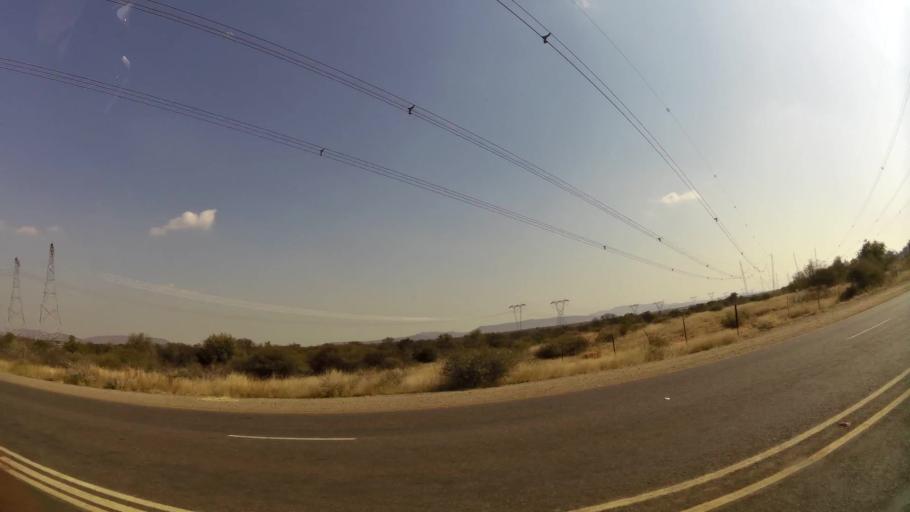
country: ZA
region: North-West
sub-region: Bojanala Platinum District Municipality
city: Mogwase
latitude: -25.3906
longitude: 27.0702
